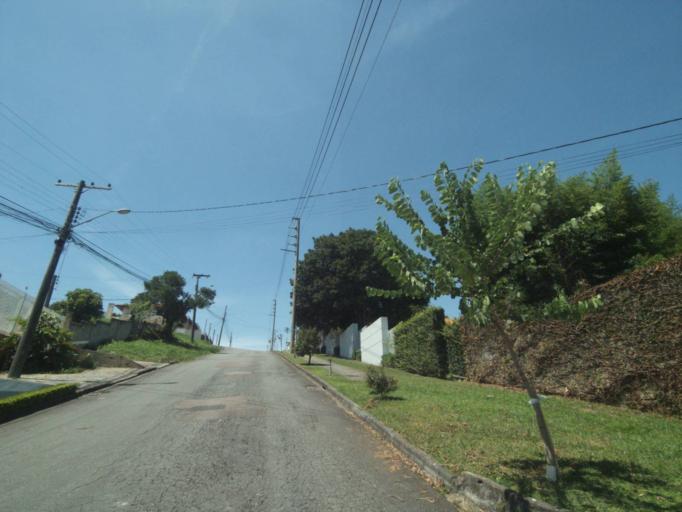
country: BR
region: Parana
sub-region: Curitiba
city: Curitiba
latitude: -25.4680
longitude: -49.2458
